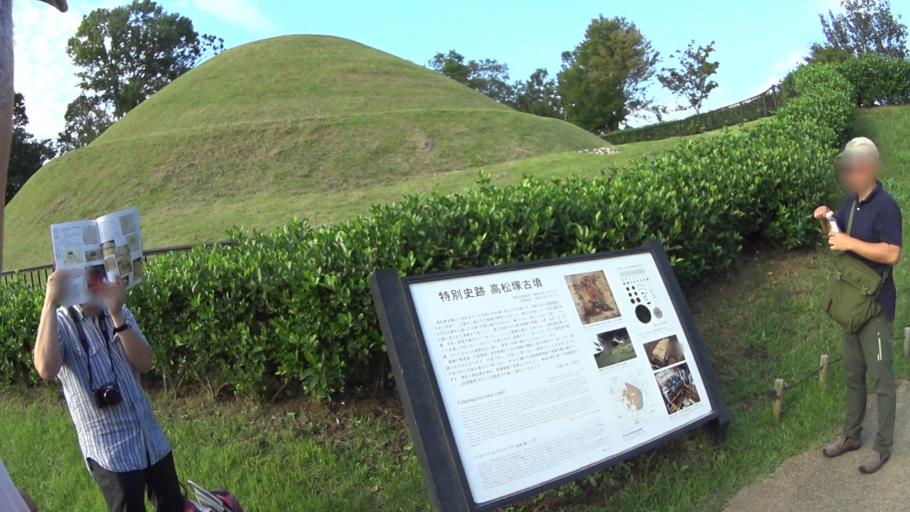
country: JP
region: Nara
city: Kashihara-shi
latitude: 34.4621
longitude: 135.8062
